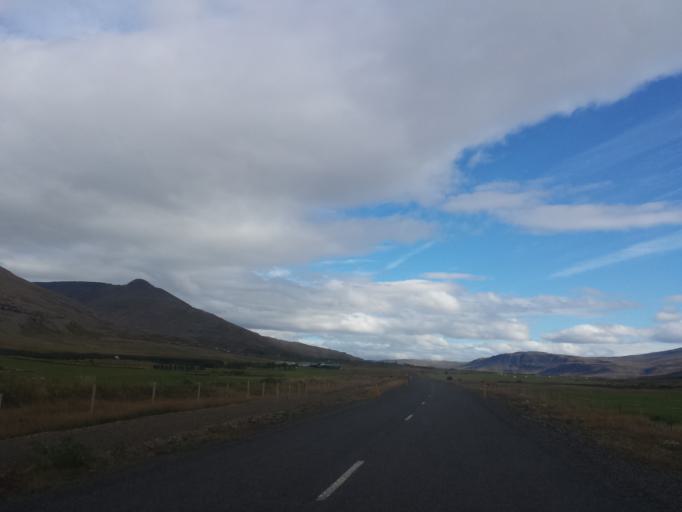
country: IS
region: Capital Region
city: Mosfellsbaer
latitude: 64.4283
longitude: -21.6826
